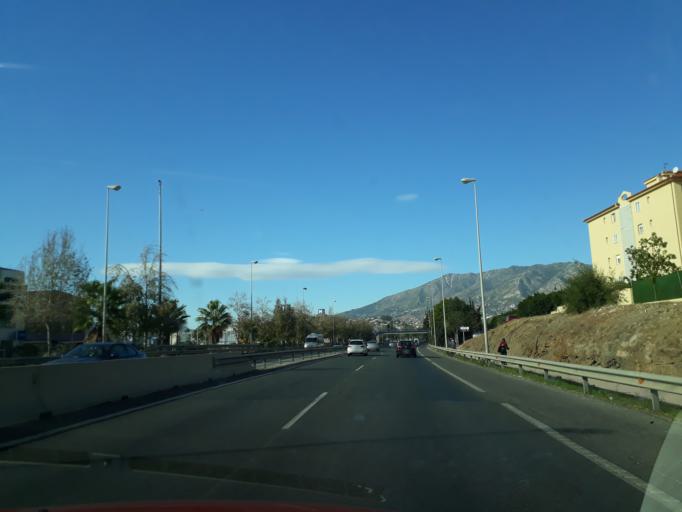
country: ES
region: Andalusia
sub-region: Provincia de Malaga
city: Fuengirola
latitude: 36.5340
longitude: -4.6324
